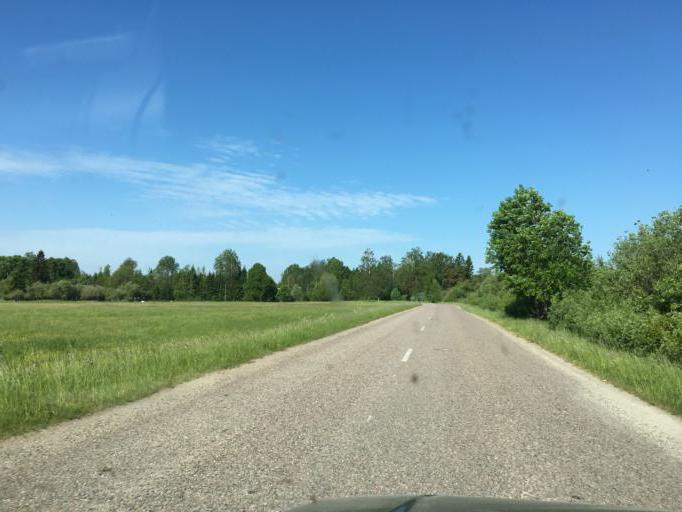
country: LV
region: Ventspils
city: Ventspils
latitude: 57.4994
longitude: 21.8309
